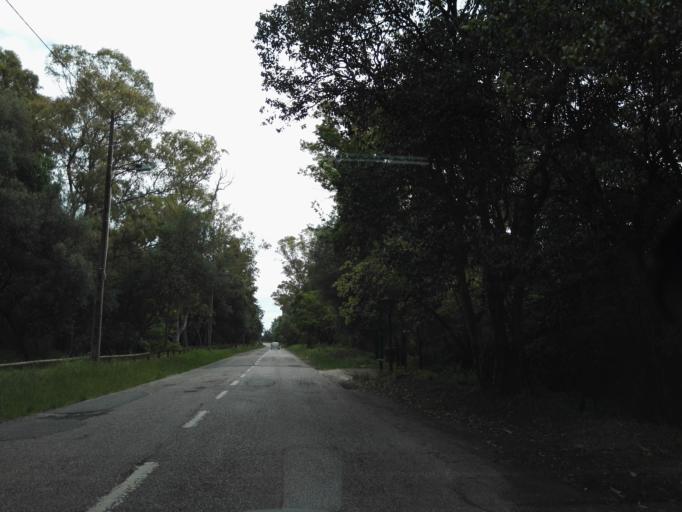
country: PT
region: Lisbon
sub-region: Amadora
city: Amadora
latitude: 38.7301
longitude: -9.2040
